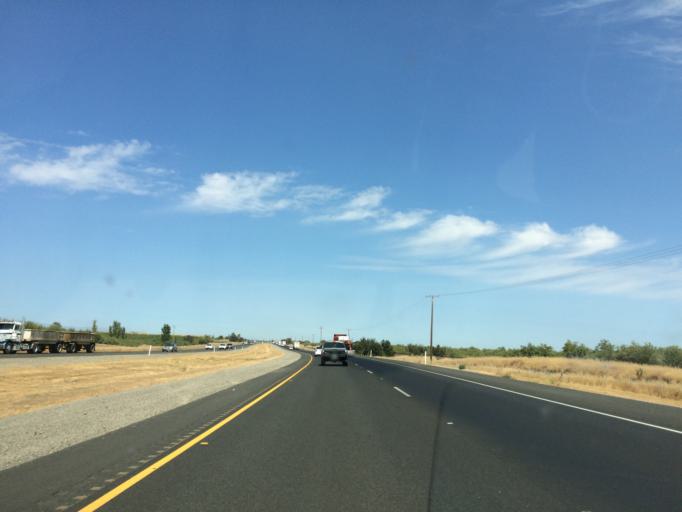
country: US
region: California
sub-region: Colusa County
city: Arbuckle
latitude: 38.9740
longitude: -122.0288
